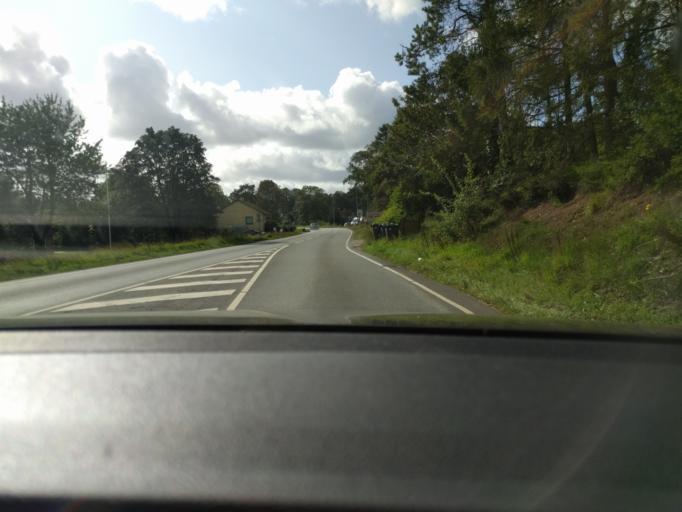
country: DK
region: Central Jutland
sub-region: Viborg Kommune
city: Bjerringbro
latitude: 56.2773
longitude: 9.6226
